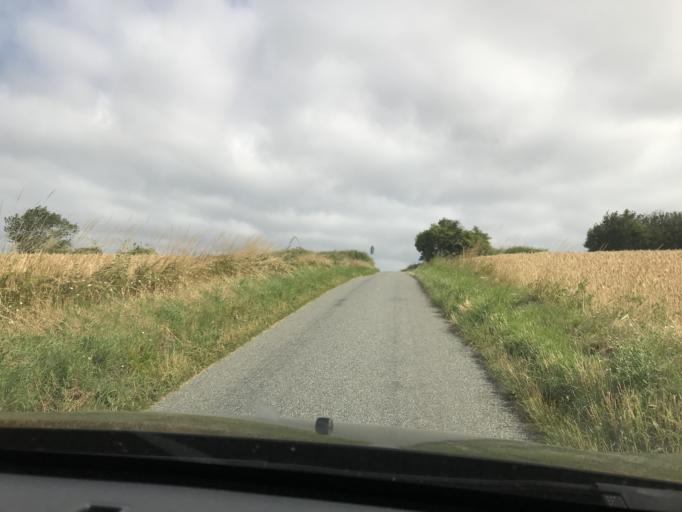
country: DK
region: South Denmark
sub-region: AEro Kommune
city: AEroskobing
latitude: 54.9255
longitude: 10.2786
